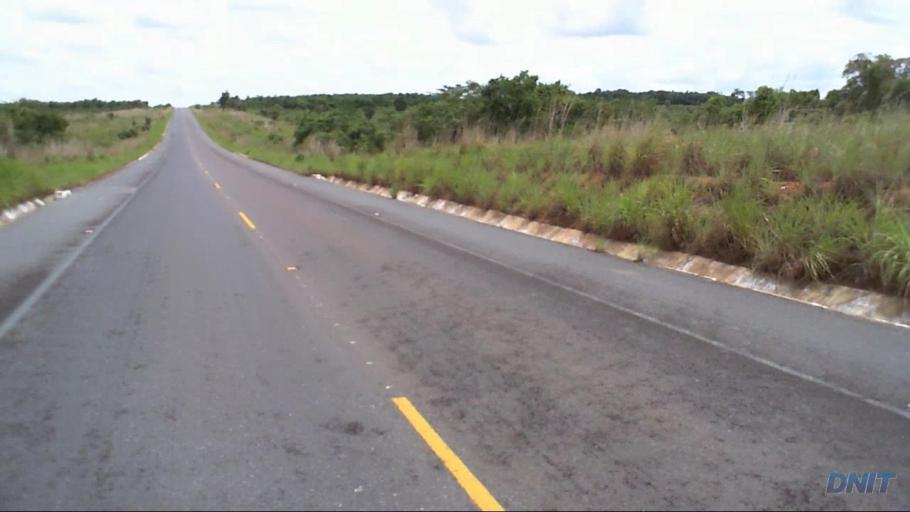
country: BR
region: Goias
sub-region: Sao Miguel Do Araguaia
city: Sao Miguel do Araguaia
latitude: -13.2966
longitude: -50.3478
